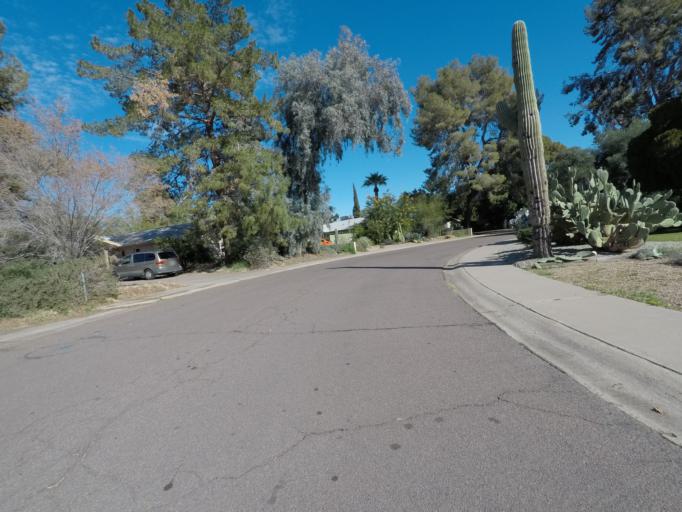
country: US
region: Arizona
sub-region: Maricopa County
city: Tempe Junction
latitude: 33.4124
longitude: -111.9490
